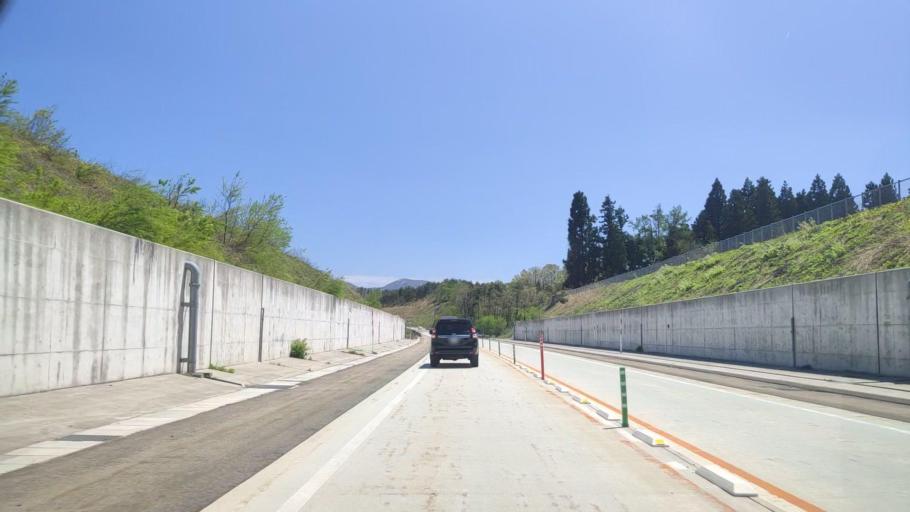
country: JP
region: Yamagata
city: Obanazawa
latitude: 38.5928
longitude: 140.3872
